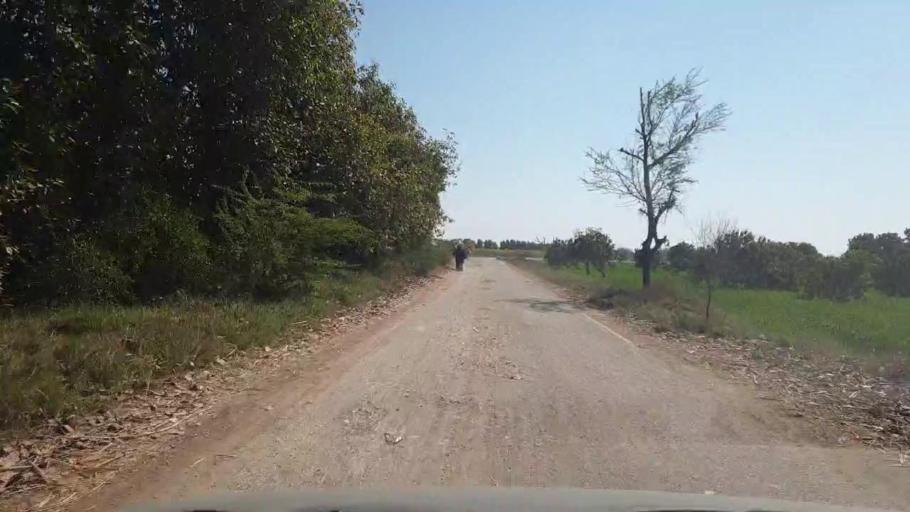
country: PK
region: Sindh
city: Mirwah Gorchani
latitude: 25.3009
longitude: 69.1236
